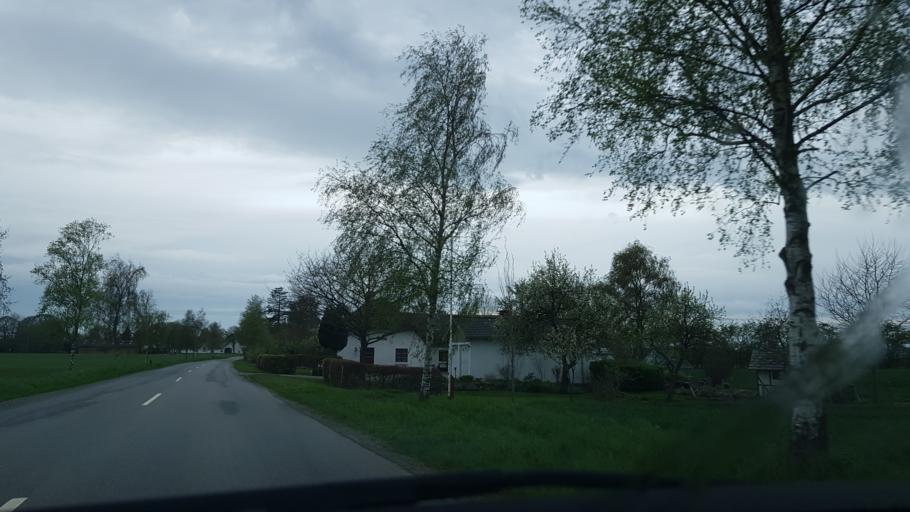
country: DK
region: South Denmark
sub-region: Kolding Kommune
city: Lunderskov
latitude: 55.4637
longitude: 9.3532
